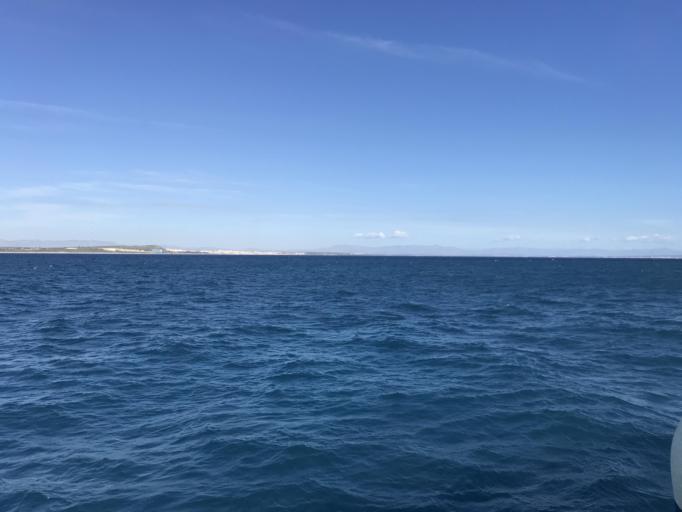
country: ES
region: Valencia
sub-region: Provincia de Alicante
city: Torrevieja
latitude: 38.0215
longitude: -0.6207
